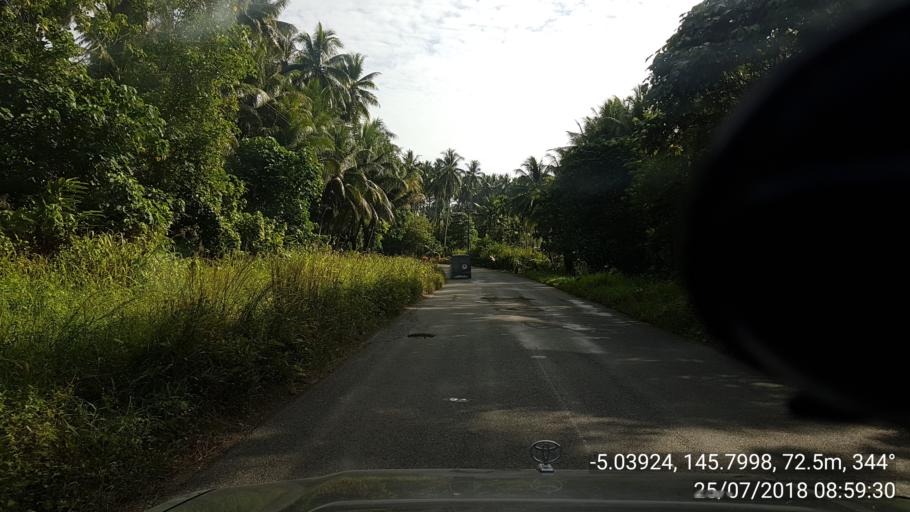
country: PG
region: Madang
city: Madang
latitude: -5.0392
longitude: 145.7997
